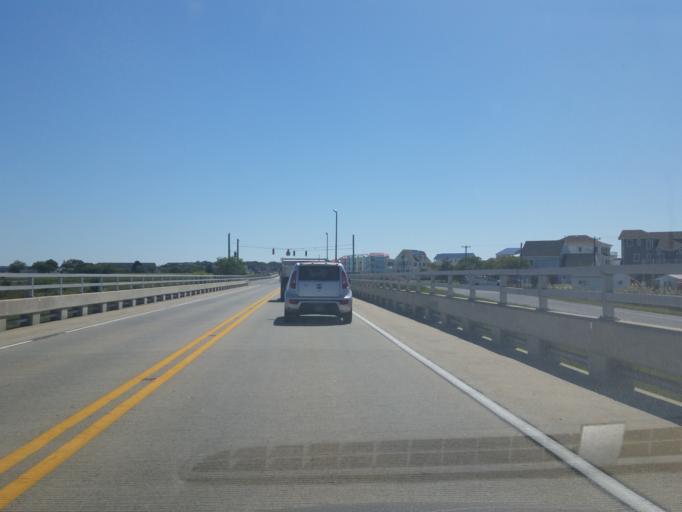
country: US
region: Delaware
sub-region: Sussex County
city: Bethany Beach
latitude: 38.4570
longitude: -75.0725
